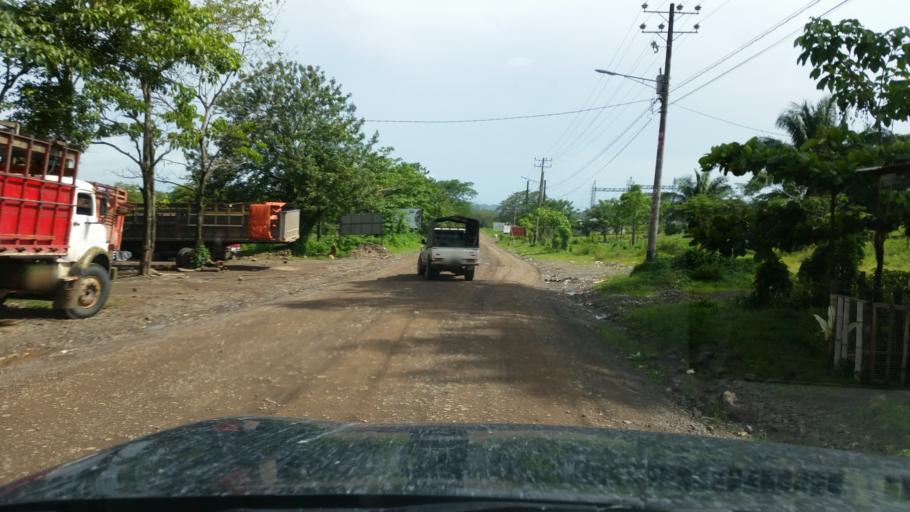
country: NI
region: Atlantico Norte (RAAN)
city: Siuna
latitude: 13.7121
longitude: -84.7751
